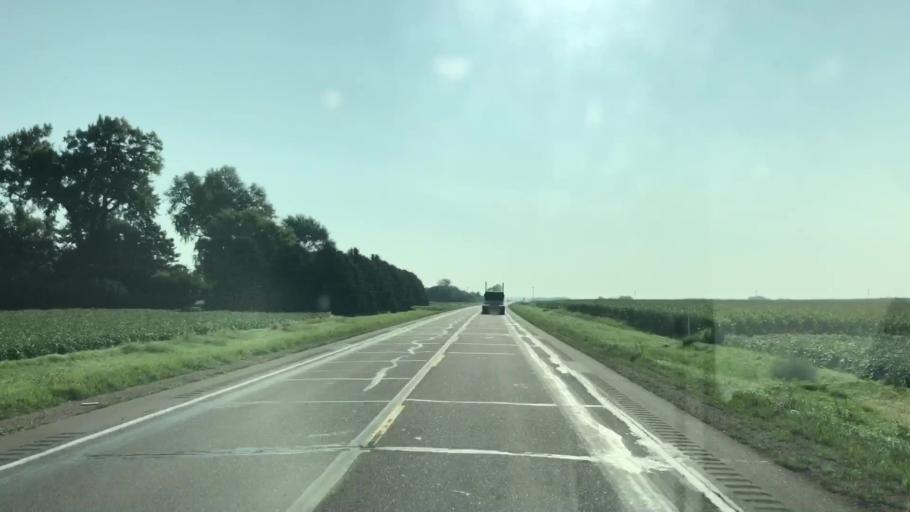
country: US
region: Iowa
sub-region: O'Brien County
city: Sheldon
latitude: 43.1861
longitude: -95.9671
